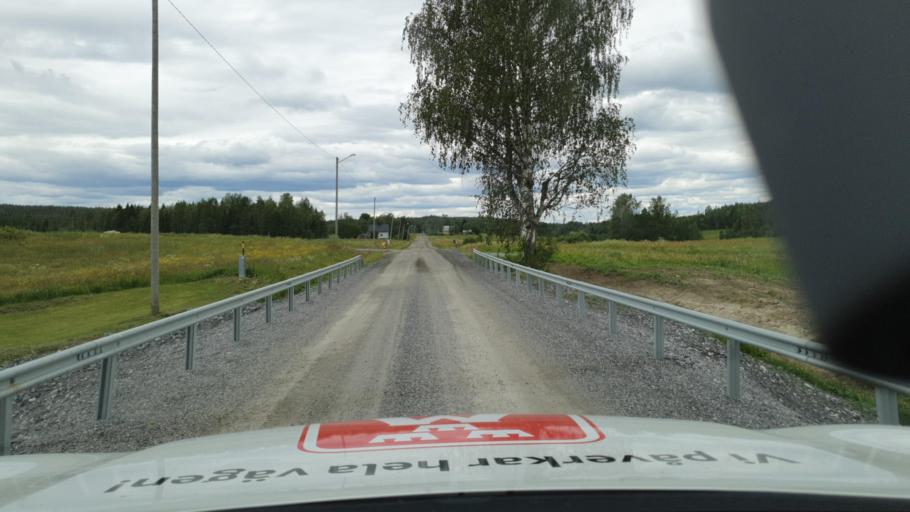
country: SE
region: Vaesterbotten
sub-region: Nordmalings Kommun
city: Nordmaling
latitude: 63.7056
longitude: 19.4387
